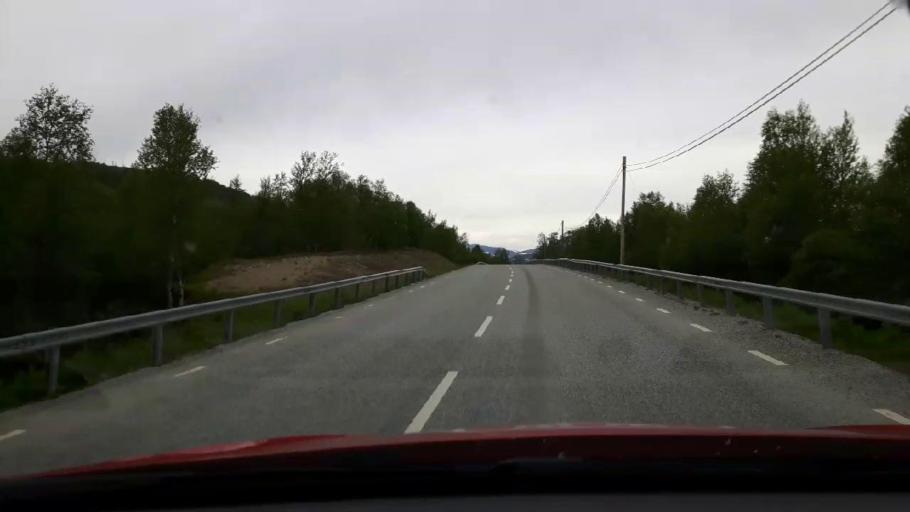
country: NO
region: Sor-Trondelag
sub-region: Tydal
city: Aas
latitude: 62.6974
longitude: 12.3978
